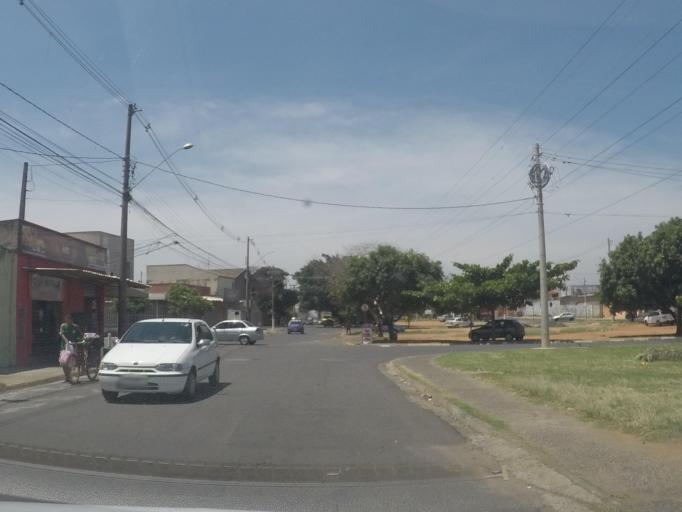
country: BR
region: Sao Paulo
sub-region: Hortolandia
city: Hortolandia
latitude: -22.8511
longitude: -47.1941
